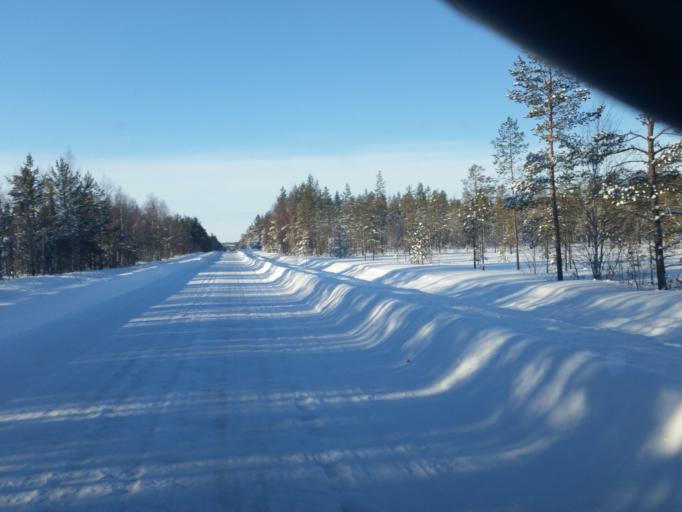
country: SE
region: Norrbotten
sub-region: Pitea Kommun
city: Roknas
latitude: 65.2000
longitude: 21.1479
